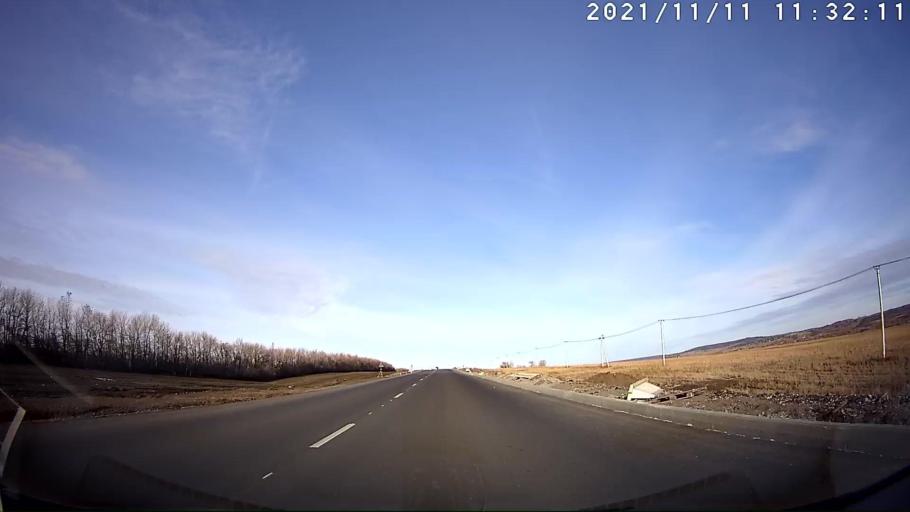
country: RU
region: Samara
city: Varlamovo
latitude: 53.3105
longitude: 48.4462
